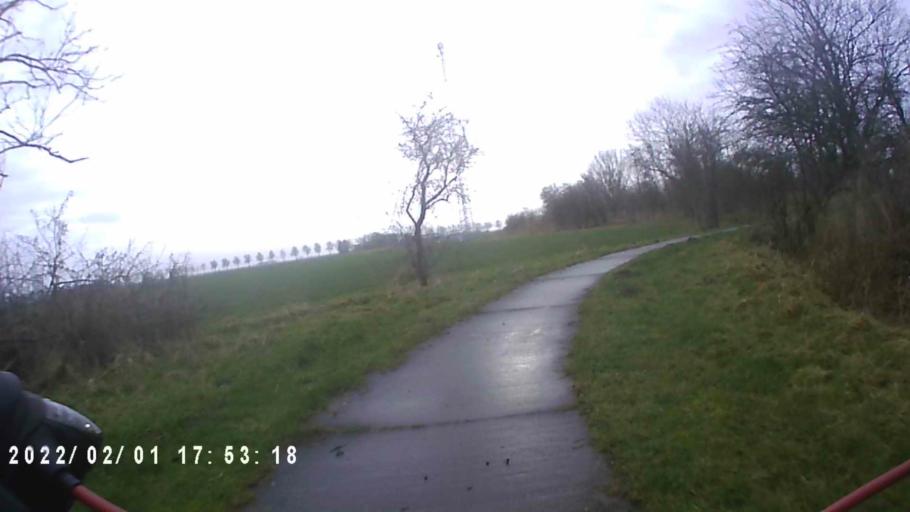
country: NL
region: Groningen
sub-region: Gemeente Zuidhorn
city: Oldehove
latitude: 53.3396
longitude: 6.3991
